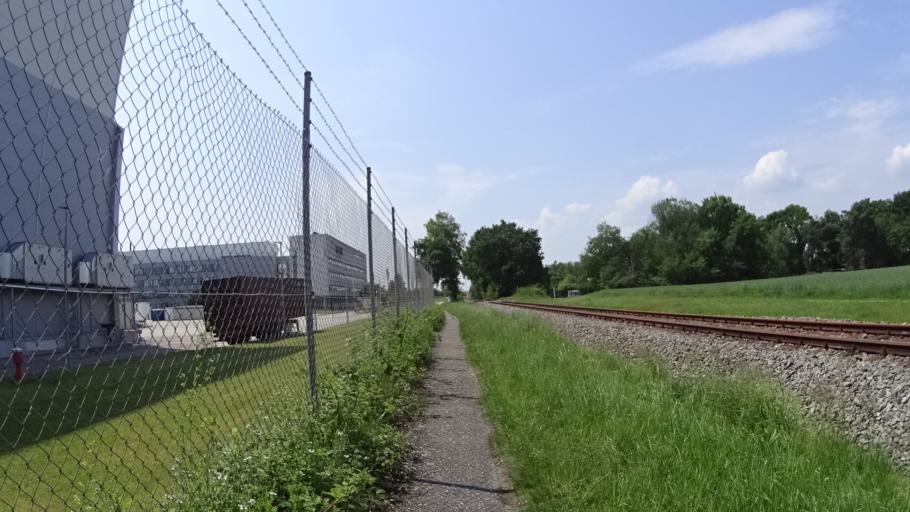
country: DE
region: Baden-Wuerttemberg
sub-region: Karlsruhe Region
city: Karlsruhe
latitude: 49.0396
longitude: 8.3656
